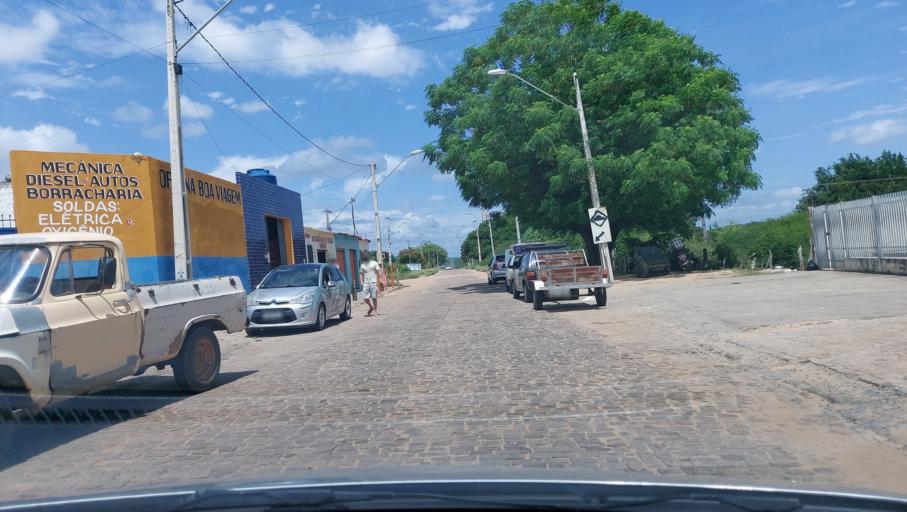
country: BR
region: Bahia
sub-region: Oliveira Dos Brejinhos
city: Beira Rio
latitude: -11.9963
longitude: -42.6285
